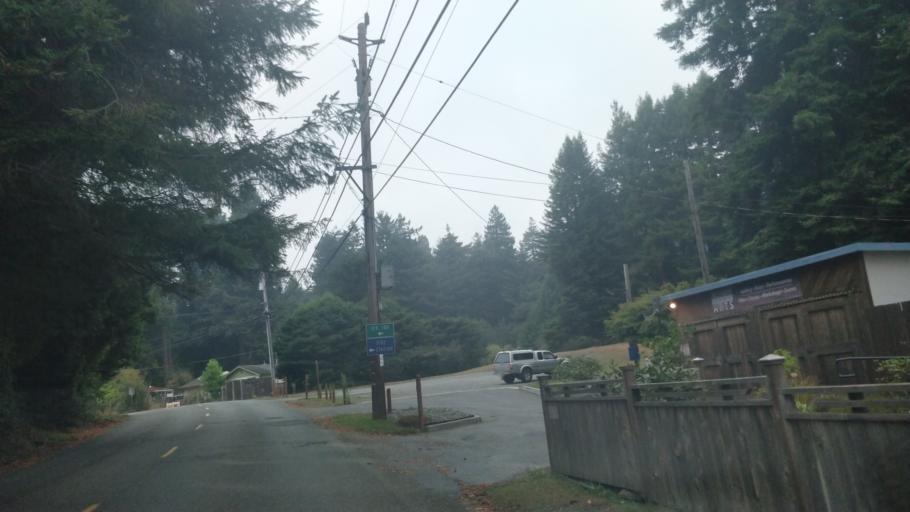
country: US
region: California
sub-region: Humboldt County
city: Westhaven-Moonstone
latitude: 41.0351
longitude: -124.1079
